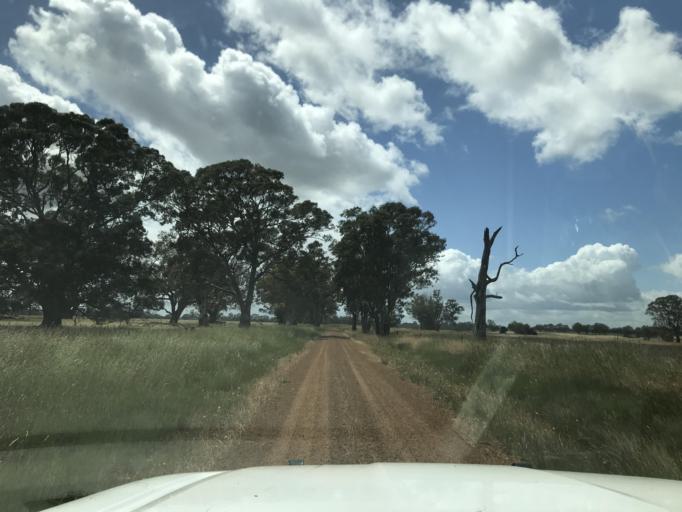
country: AU
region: South Australia
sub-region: Wattle Range
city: Penola
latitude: -37.1841
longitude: 141.4708
